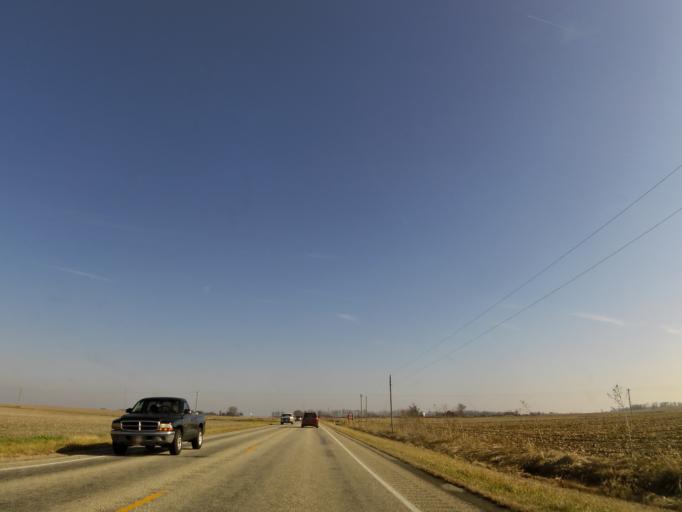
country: US
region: Indiana
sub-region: Rush County
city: Rushville
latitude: 39.5822
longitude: -85.5580
